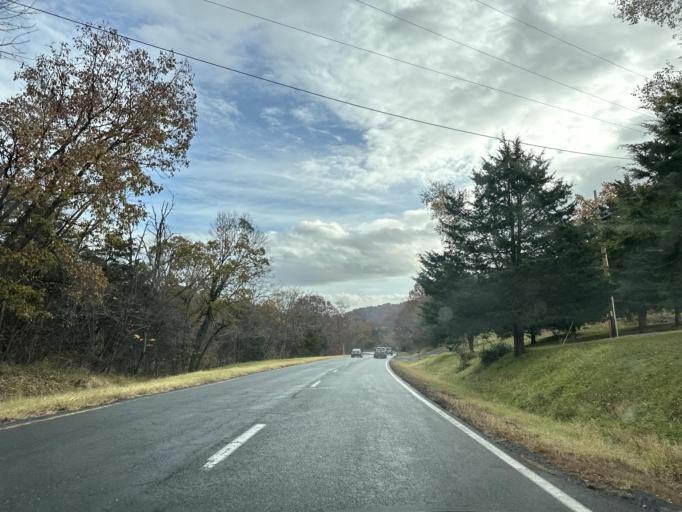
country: US
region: Virginia
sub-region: Shenandoah County
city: Strasburg
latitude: 38.9750
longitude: -78.3972
